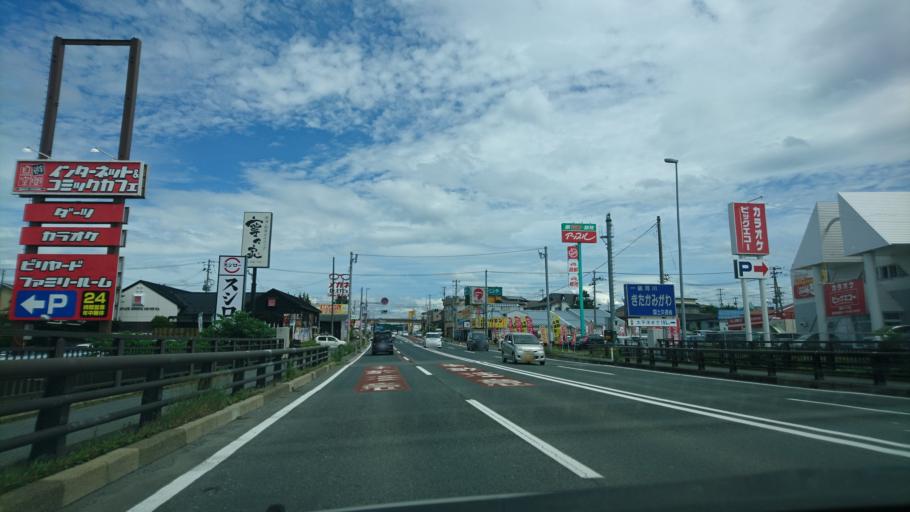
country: JP
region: Iwate
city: Morioka-shi
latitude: 39.7244
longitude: 141.1289
